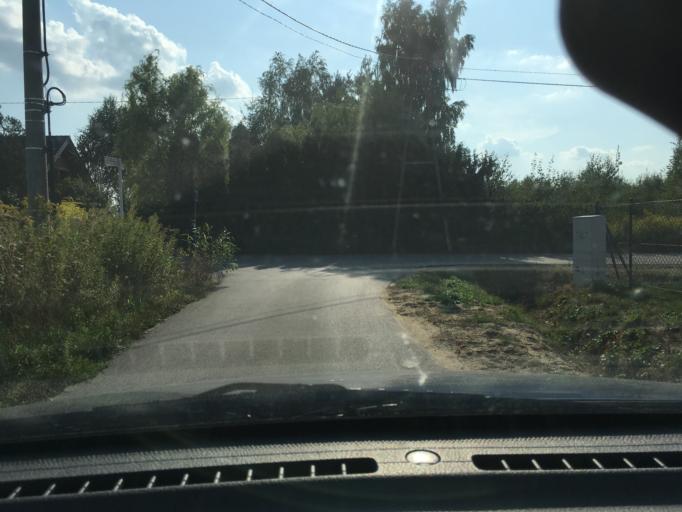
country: PL
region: Masovian Voivodeship
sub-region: Powiat piaseczynski
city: Lesznowola
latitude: 52.0516
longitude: 20.9323
